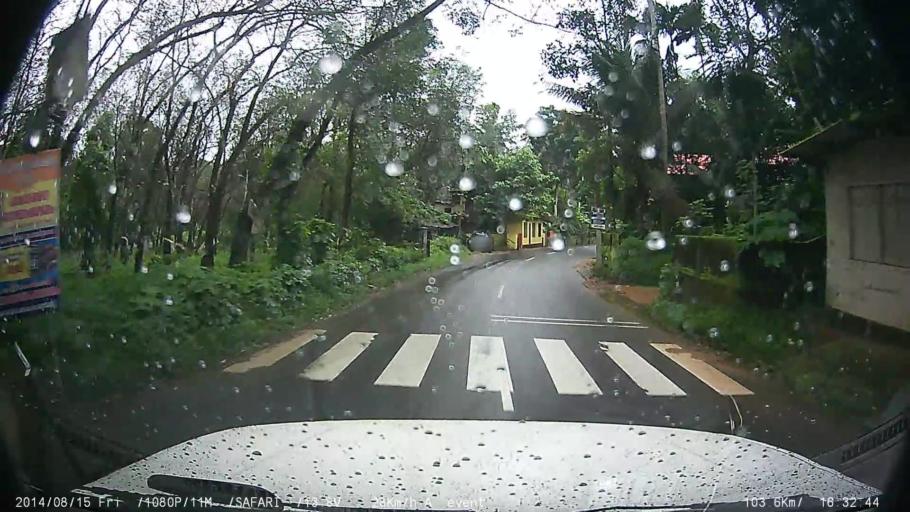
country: IN
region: Kerala
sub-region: Kottayam
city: Palackattumala
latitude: 9.7332
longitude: 76.6309
